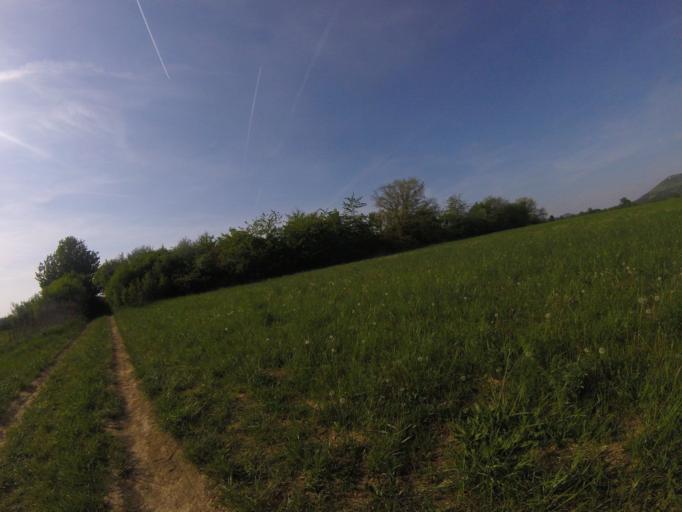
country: HU
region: Pest
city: Solymar
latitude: 47.6025
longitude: 18.9364
